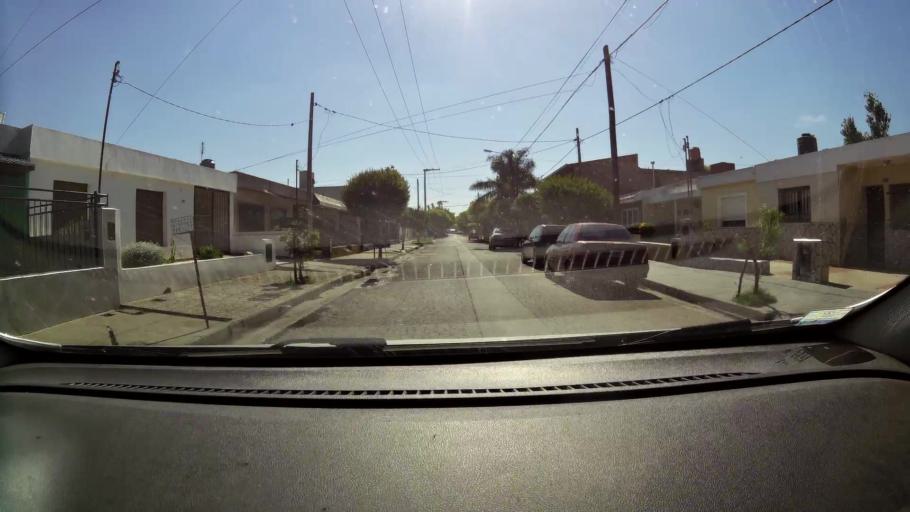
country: AR
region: Cordoba
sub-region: Departamento de Capital
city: Cordoba
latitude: -31.3607
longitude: -64.1693
